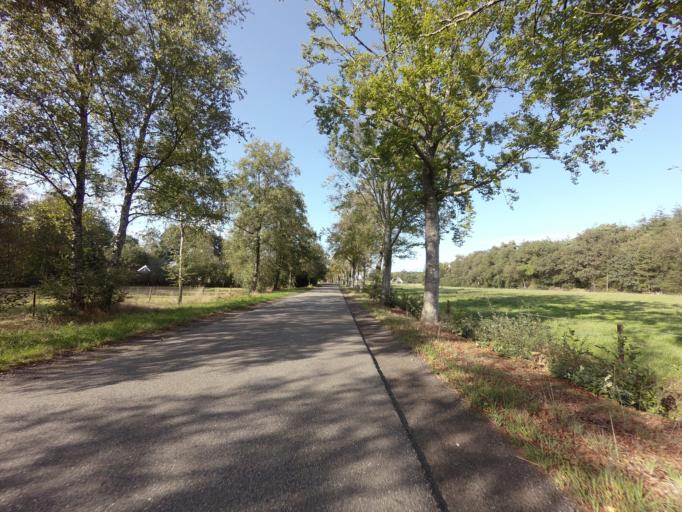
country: NL
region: Friesland
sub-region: Gemeente Heerenveen
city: Jubbega
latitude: 53.0051
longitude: 6.2320
